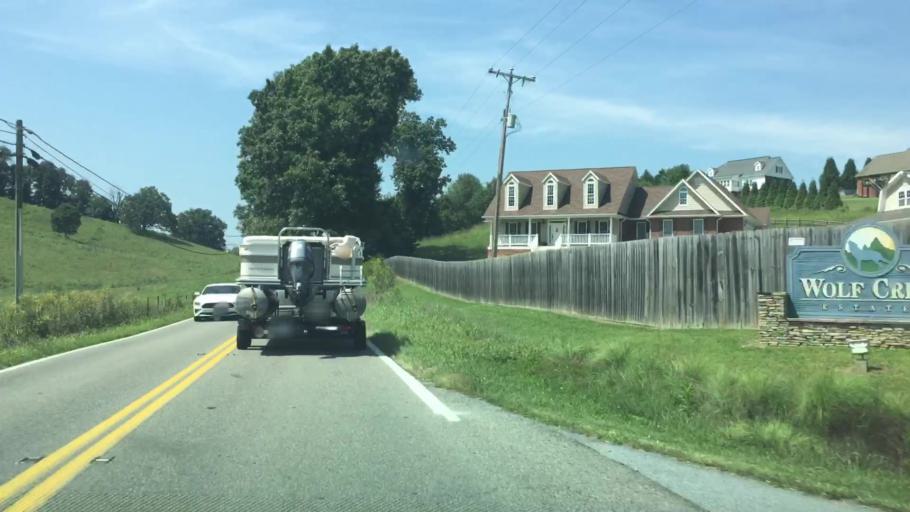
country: US
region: Virginia
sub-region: Washington County
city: Abingdon
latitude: 36.6547
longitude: -81.9773
